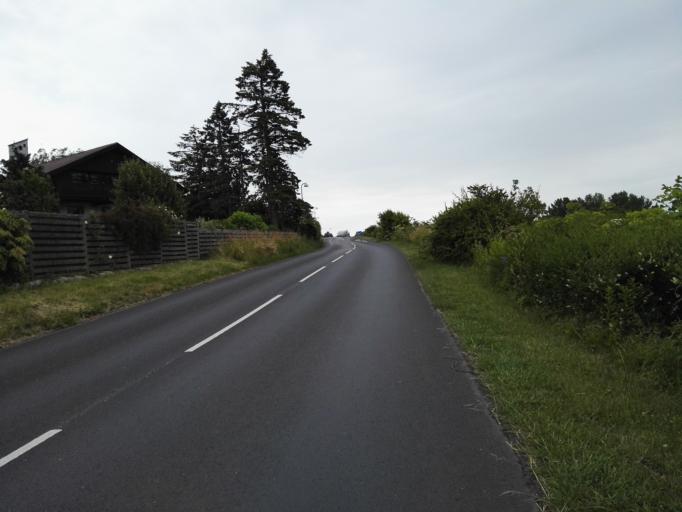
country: DK
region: Zealand
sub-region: Roskilde Kommune
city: Jyllinge
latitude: 55.7600
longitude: 12.0973
